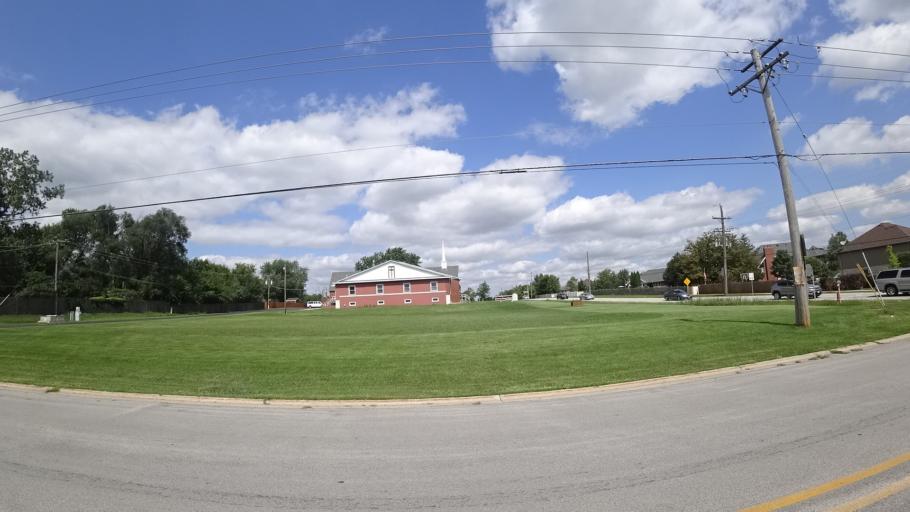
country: US
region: Illinois
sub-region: Cook County
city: Orland Hills
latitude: 41.5723
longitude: -87.8473
